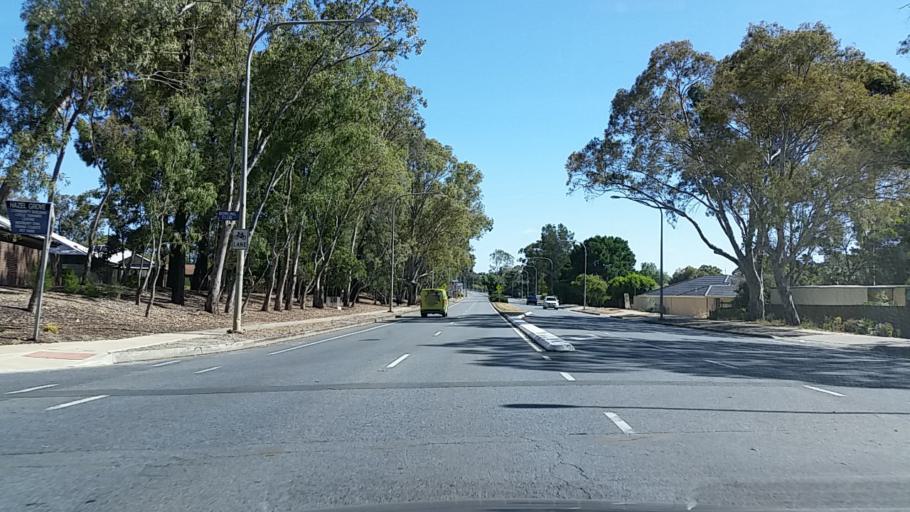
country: AU
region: South Australia
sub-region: Tea Tree Gully
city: Hope Valley
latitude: -34.8223
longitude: 138.6947
